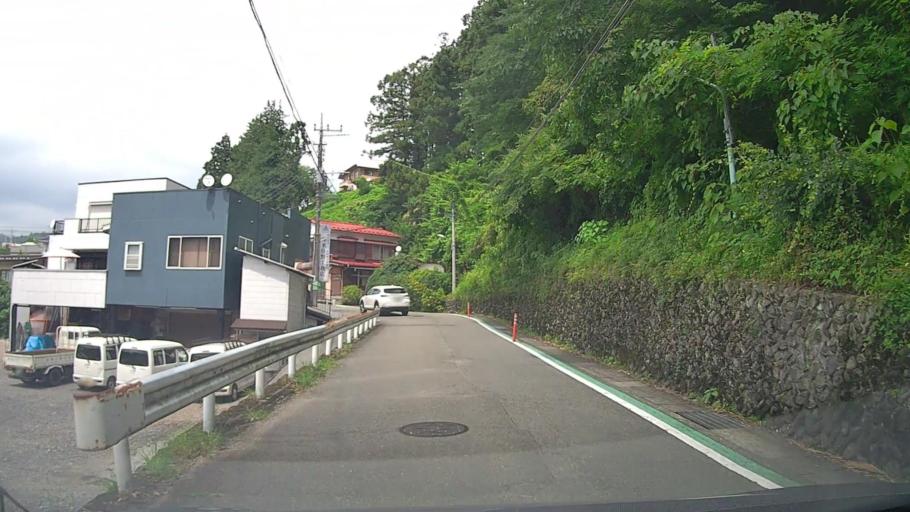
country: JP
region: Tokyo
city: Itsukaichi
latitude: 35.7253
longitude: 139.2213
